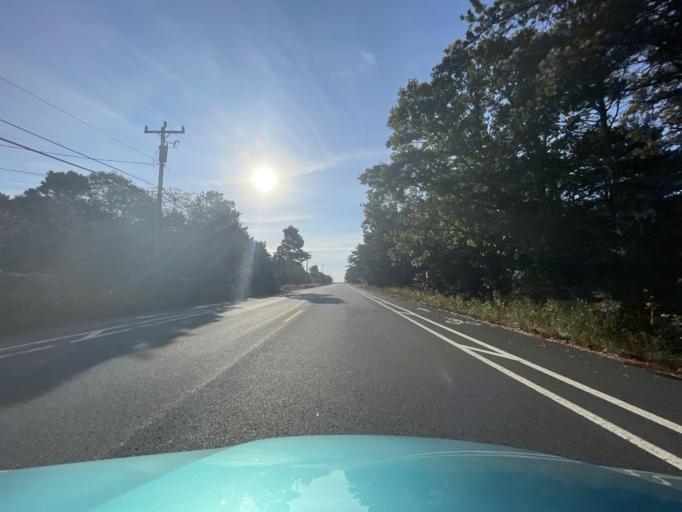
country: US
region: Massachusetts
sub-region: Bristol County
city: Head of Westport
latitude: 41.5029
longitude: -71.0403
